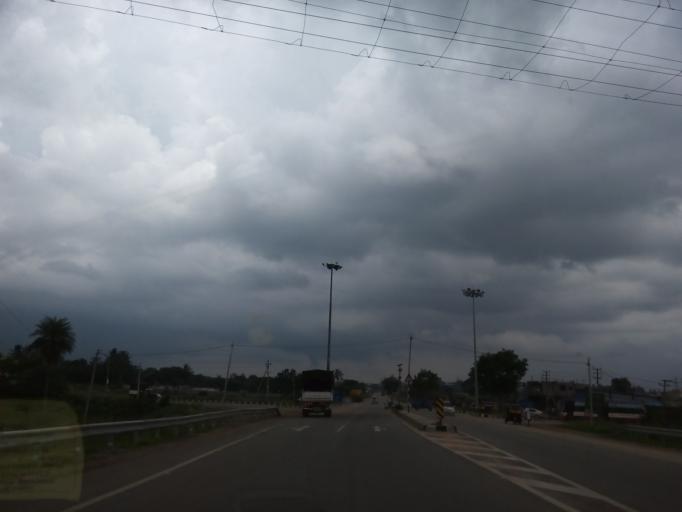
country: IN
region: Karnataka
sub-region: Hassan
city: Hassan
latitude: 12.9899
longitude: 76.0944
